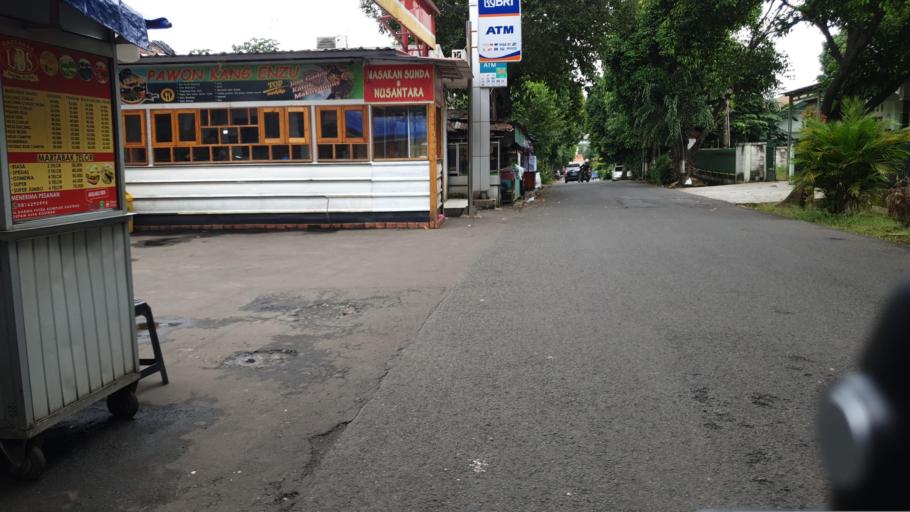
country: ID
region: Jakarta Raya
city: Jakarta
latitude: -6.2548
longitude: 106.7837
